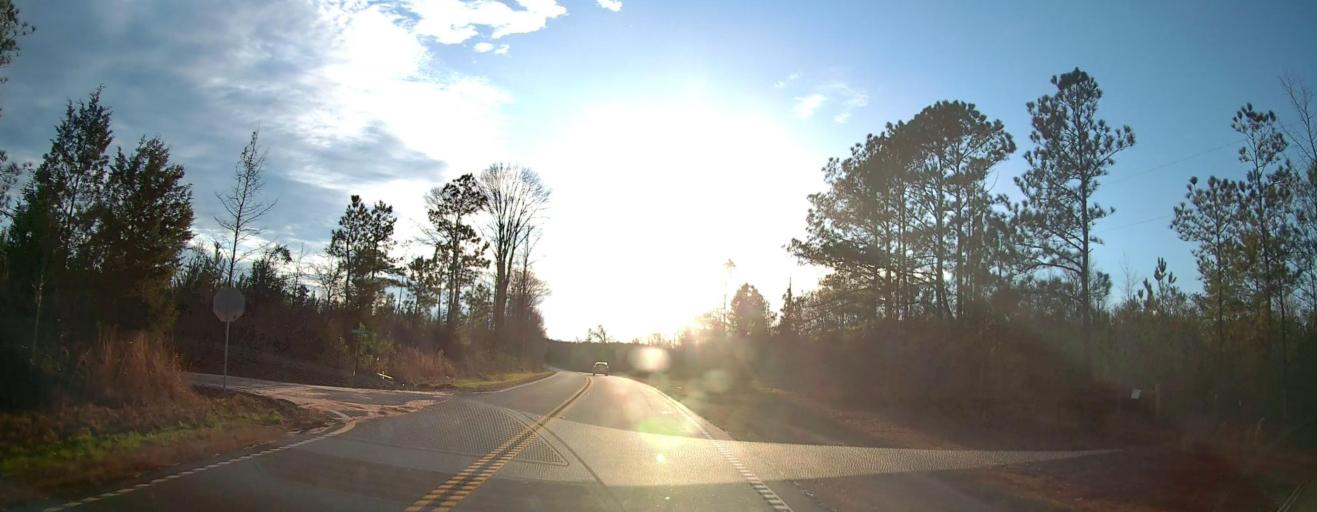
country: US
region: Georgia
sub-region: Talbot County
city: Sardis
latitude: 32.7186
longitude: -84.6758
